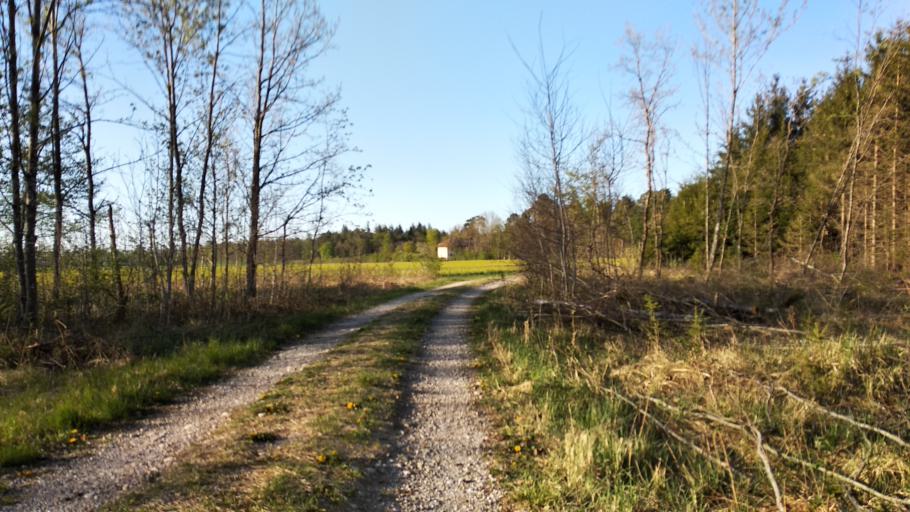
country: DE
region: Bavaria
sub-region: Upper Bavaria
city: Grasbrunn
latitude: 48.0950
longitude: 11.7375
